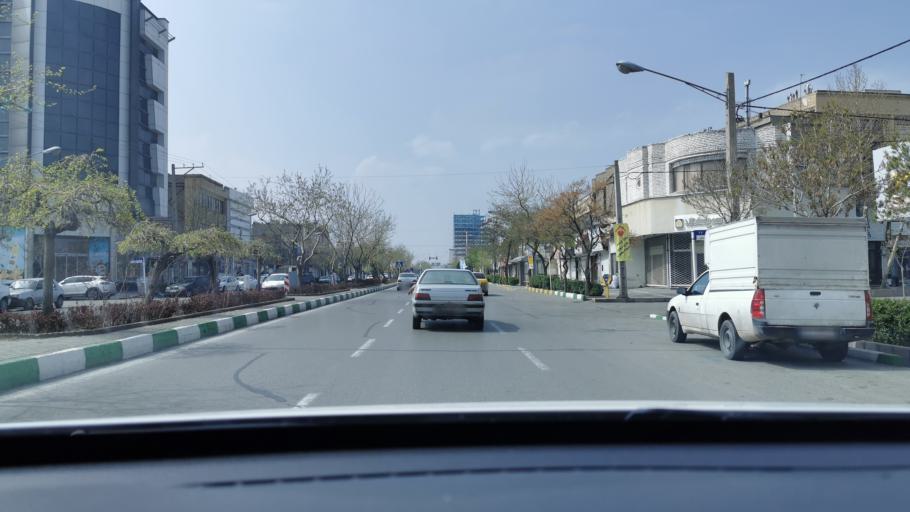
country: IR
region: Razavi Khorasan
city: Mashhad
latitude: 36.3304
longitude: 59.5223
